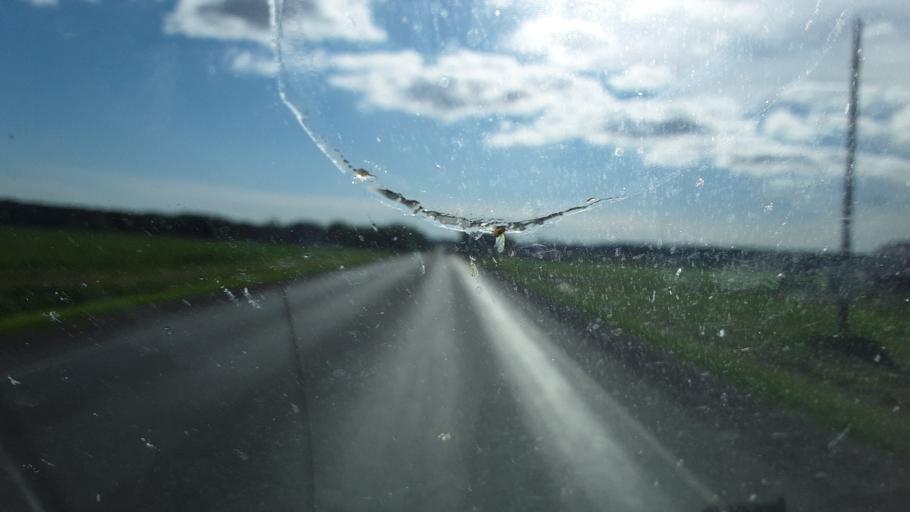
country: US
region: Wisconsin
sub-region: Marathon County
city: Spencer
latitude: 44.6562
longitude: -90.3378
